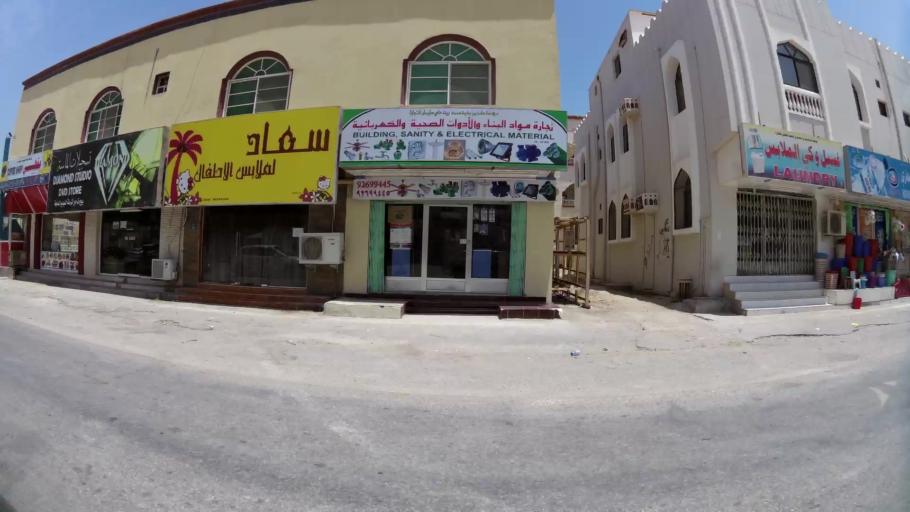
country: OM
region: Zufar
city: Salalah
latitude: 17.0173
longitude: 54.0826
